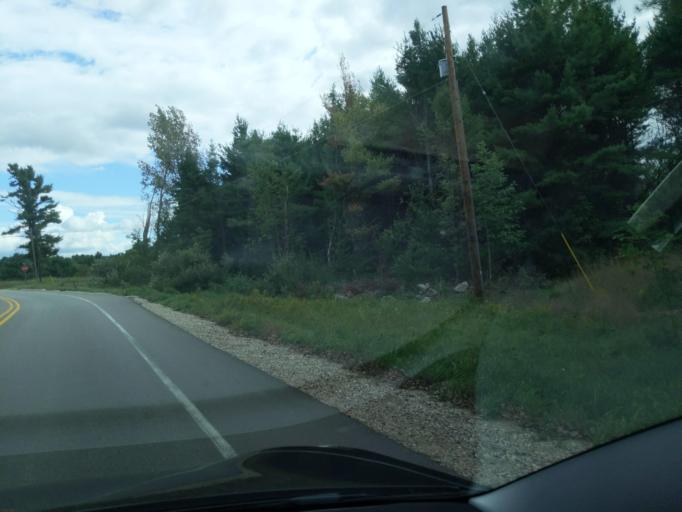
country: US
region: Michigan
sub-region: Kalkaska County
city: Rapid City
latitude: 44.8938
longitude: -85.2733
